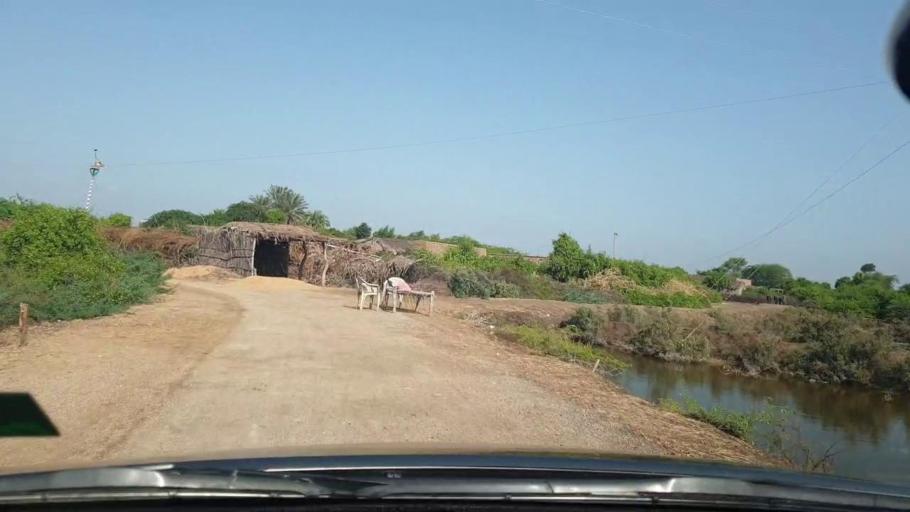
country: PK
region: Sindh
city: Tando Bago
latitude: 24.6871
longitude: 69.0091
